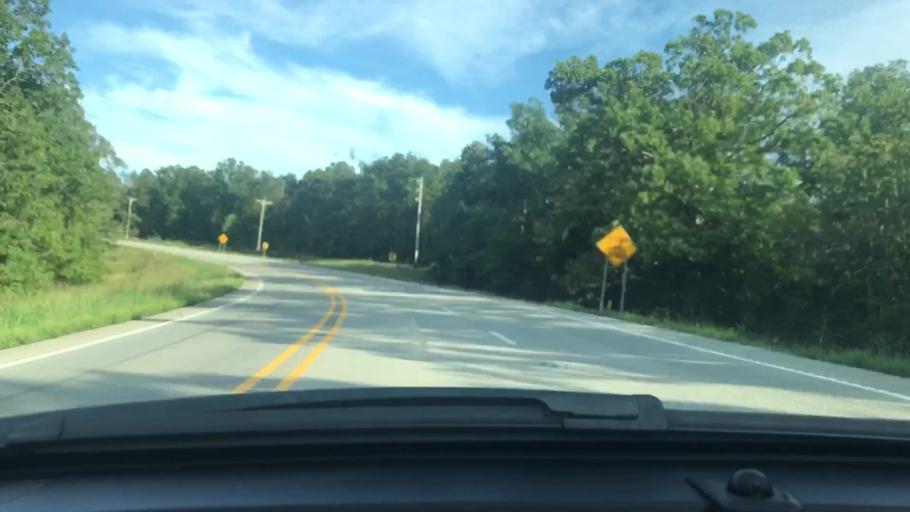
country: US
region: Arkansas
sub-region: Sharp County
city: Cherokee Village
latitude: 36.2743
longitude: -91.3215
